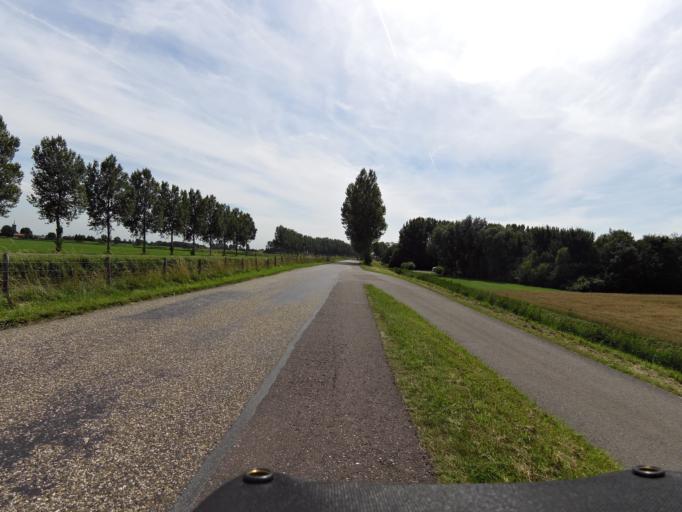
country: NL
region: South Holland
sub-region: Gemeente Goeree-Overflakkee
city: Dirksland
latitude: 51.7597
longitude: 4.1056
